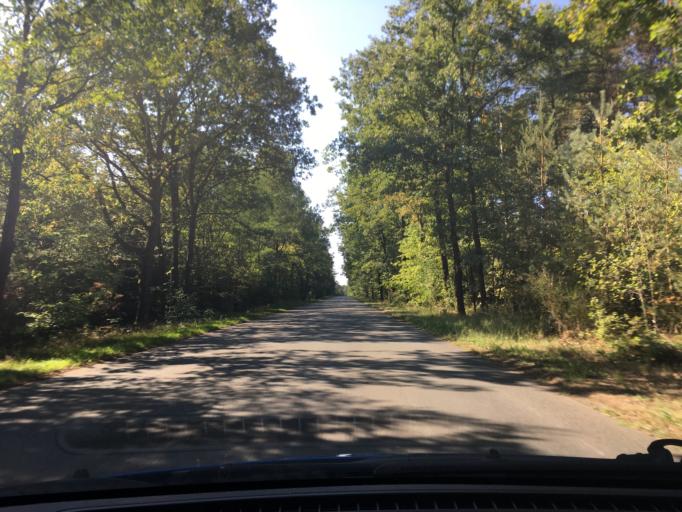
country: DE
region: Lower Saxony
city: Munster
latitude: 52.9631
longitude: 10.1332
